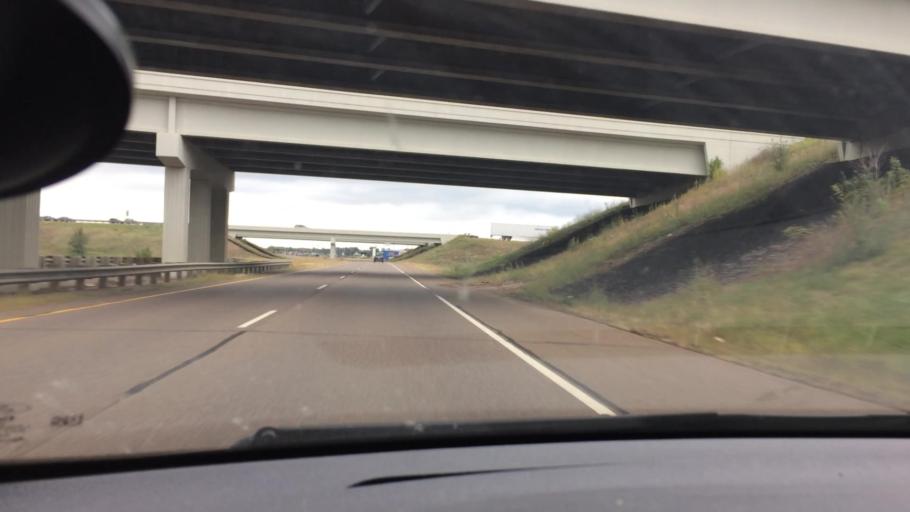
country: US
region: Wisconsin
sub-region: Chippewa County
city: Lake Hallie
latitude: 44.8917
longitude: -91.4189
